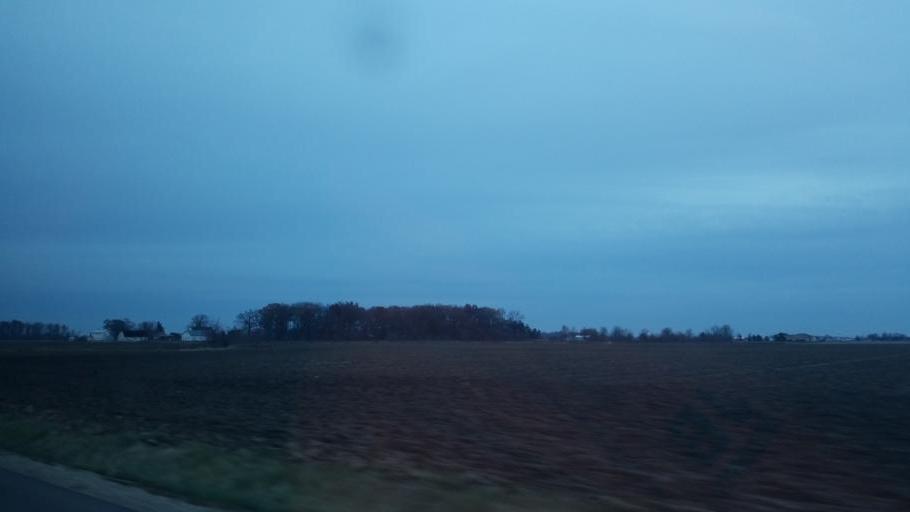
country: US
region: Indiana
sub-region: Adams County
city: Berne
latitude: 40.7396
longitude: -84.9948
